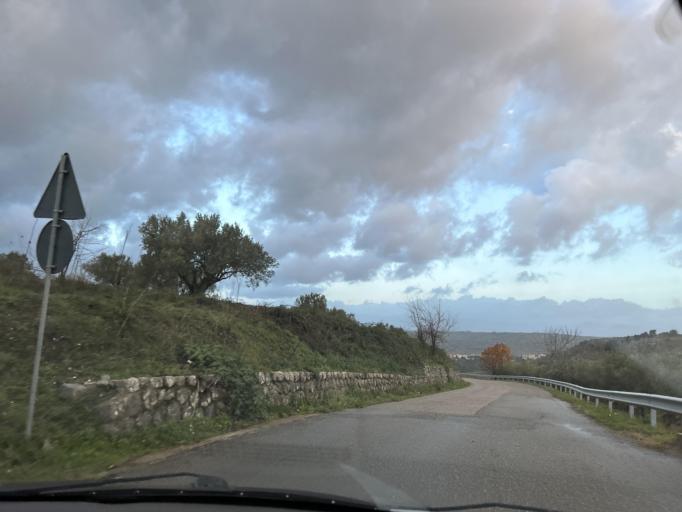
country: IT
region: Calabria
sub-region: Provincia di Catanzaro
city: Montauro
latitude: 38.7651
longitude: 16.5169
